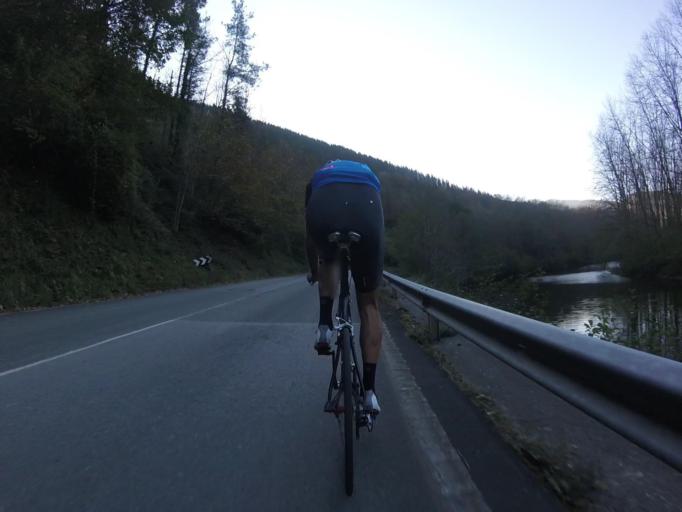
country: ES
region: Navarre
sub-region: Provincia de Navarra
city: Igantzi
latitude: 43.2329
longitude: -1.6735
